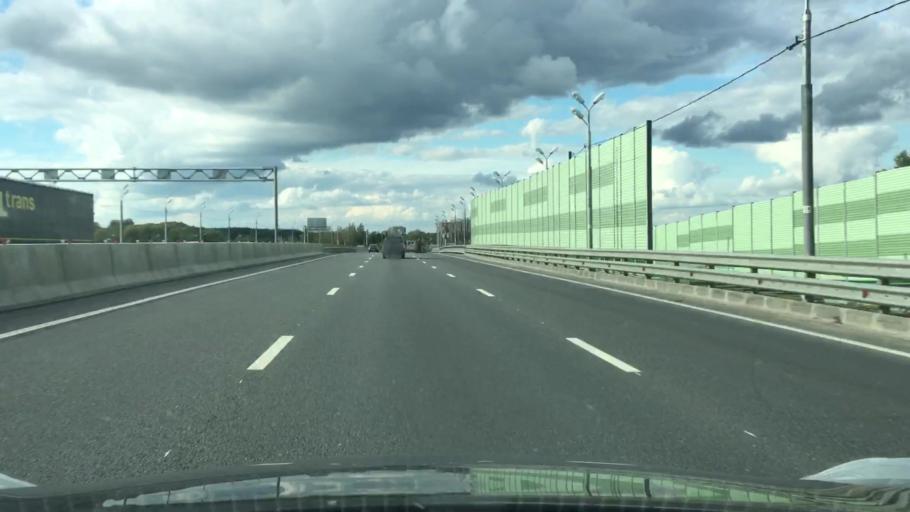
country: RU
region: Tverskaya
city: Tver
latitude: 56.8327
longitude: 35.8017
